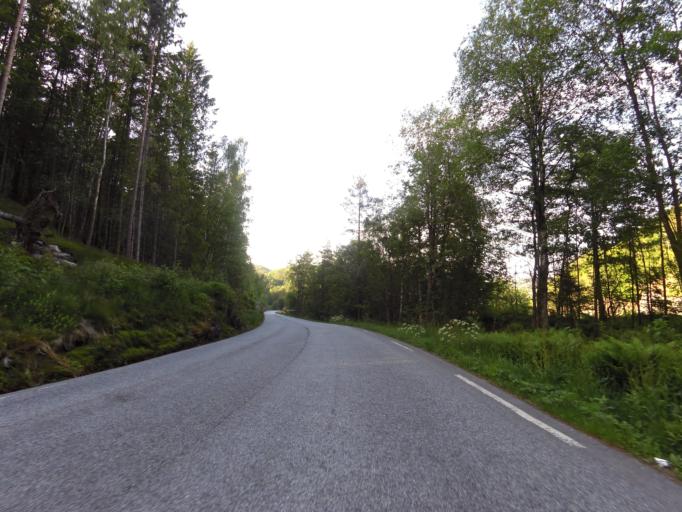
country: NO
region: Vest-Agder
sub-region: Flekkefjord
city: Flekkefjord
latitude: 58.2795
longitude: 6.6394
